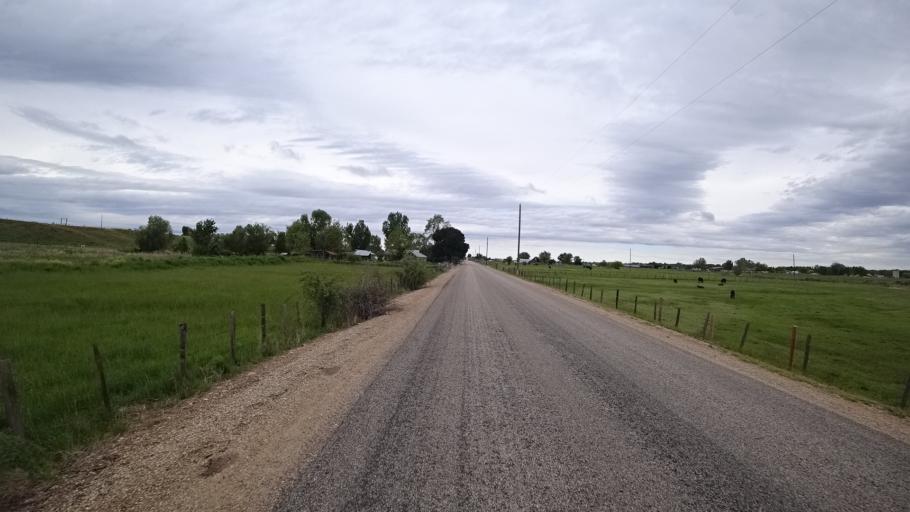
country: US
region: Idaho
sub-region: Ada County
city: Star
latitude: 43.6703
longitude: -116.4874
